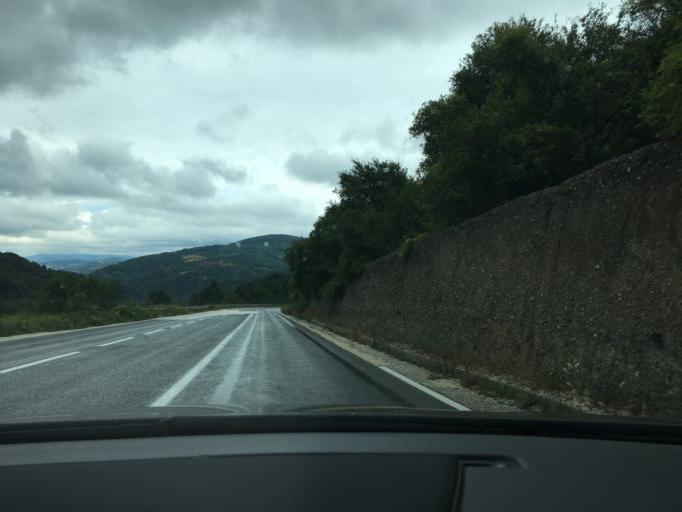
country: MK
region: Kriva Palanka
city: Kriva Palanka
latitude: 42.2185
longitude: 22.4356
